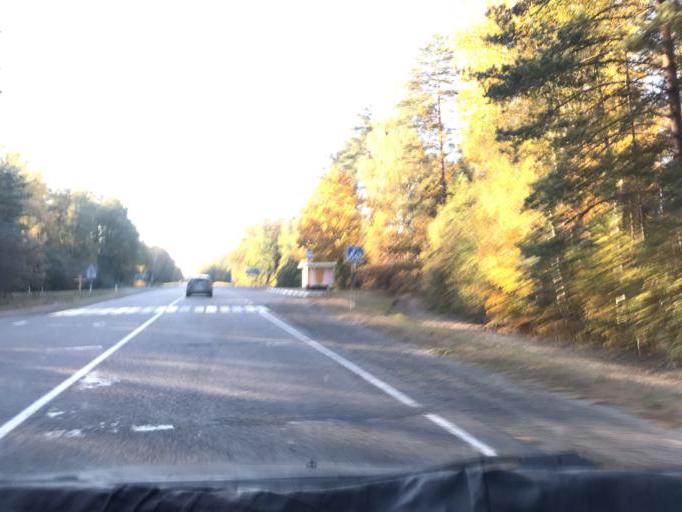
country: BY
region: Gomel
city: Pyetrykaw
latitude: 52.2716
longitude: 28.2726
